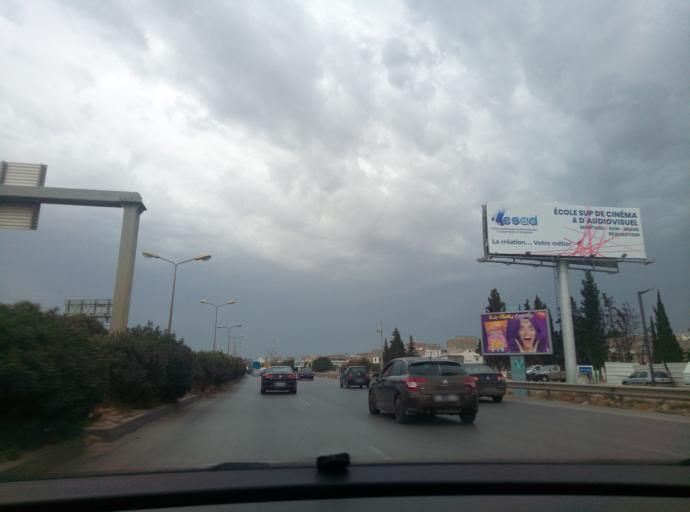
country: TN
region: Bin 'Arus
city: Ben Arous
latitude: 36.7556
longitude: 10.2017
